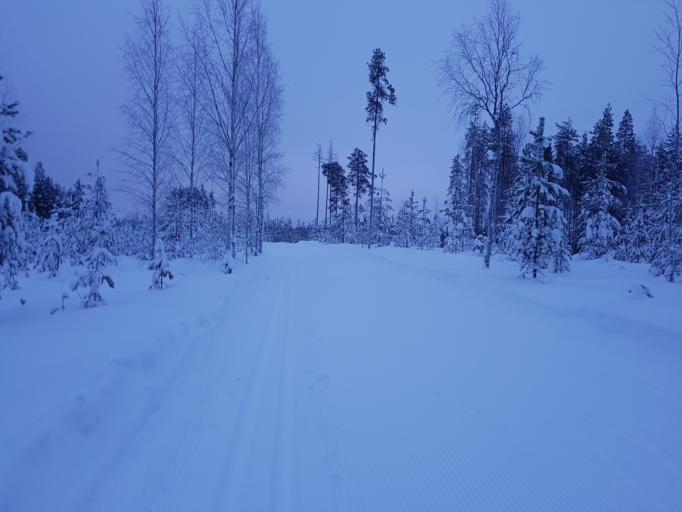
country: FI
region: Kainuu
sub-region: Kehys-Kainuu
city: Kuhmo
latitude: 64.0874
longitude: 29.5157
